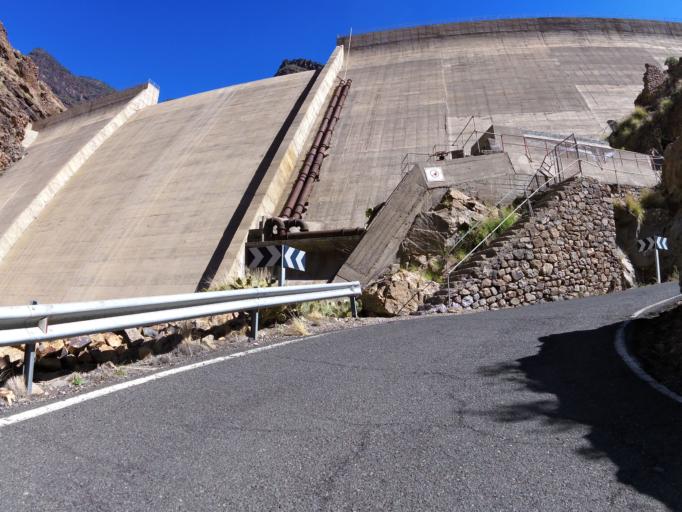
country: ES
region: Canary Islands
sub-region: Provincia de Las Palmas
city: Artenara
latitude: 27.9925
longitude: -15.7062
